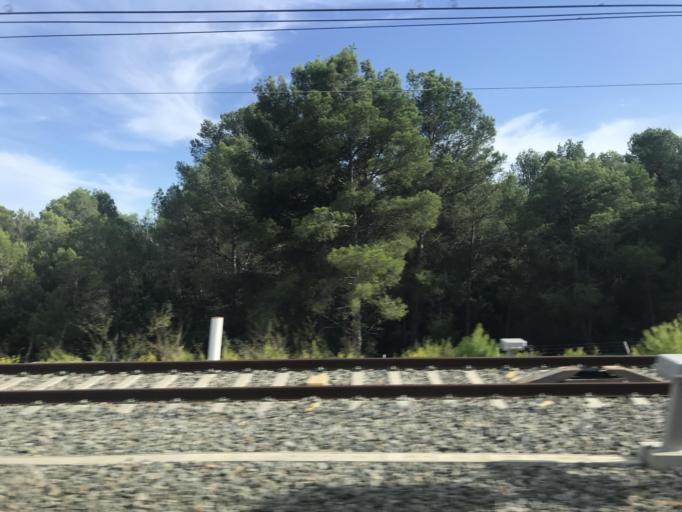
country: ES
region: Catalonia
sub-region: Provincia de Tarragona
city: Vilanova d'Escornalbou
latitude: 41.0459
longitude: 0.9678
